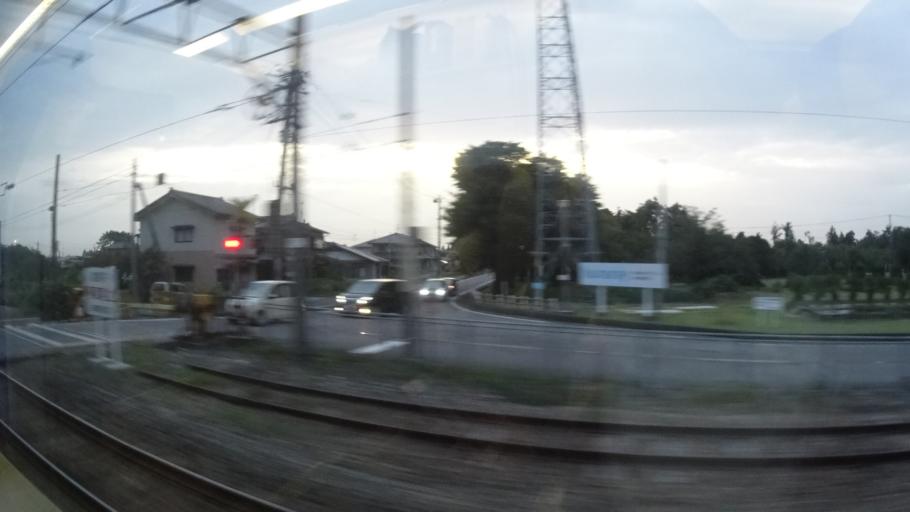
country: JP
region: Niigata
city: Shibata
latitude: 38.0623
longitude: 139.4063
